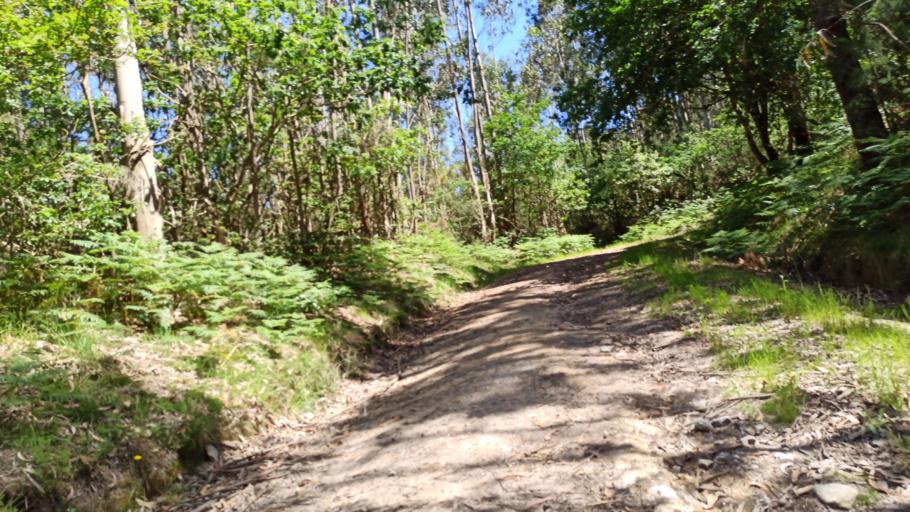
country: ES
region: Galicia
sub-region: Provincia da Coruna
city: Negreira
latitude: 42.9208
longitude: -8.7202
